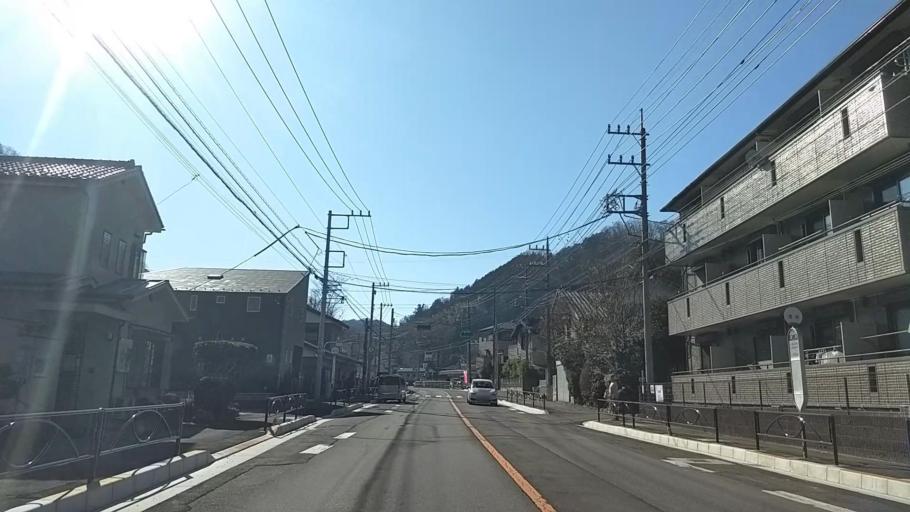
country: JP
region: Tokyo
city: Hachioji
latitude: 35.6372
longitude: 139.2709
